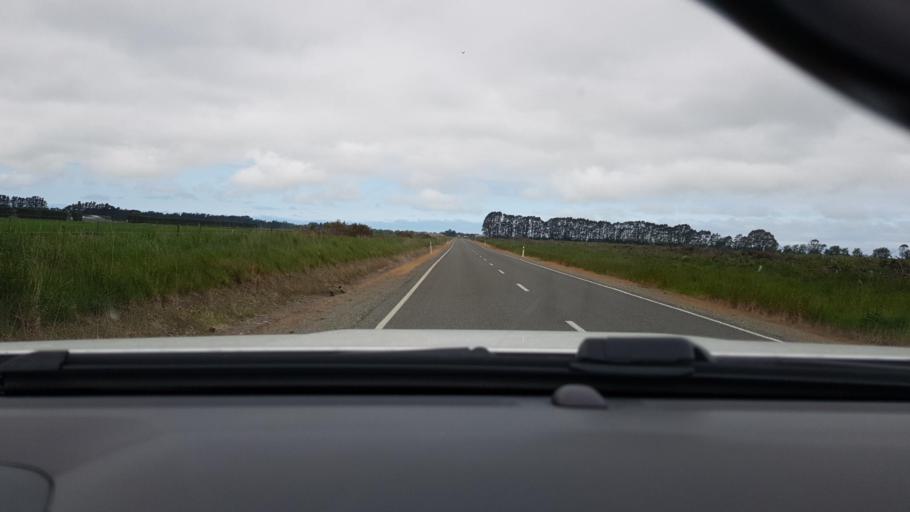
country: NZ
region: Otago
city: Oamaru
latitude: -44.9645
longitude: 171.0485
